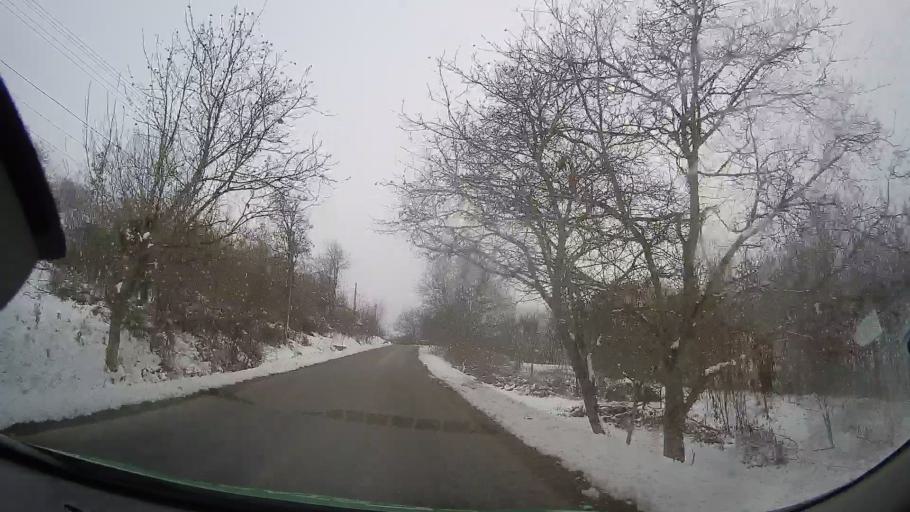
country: RO
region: Bacau
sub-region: Comuna Vultureni
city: Vultureni
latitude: 46.3854
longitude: 27.2777
